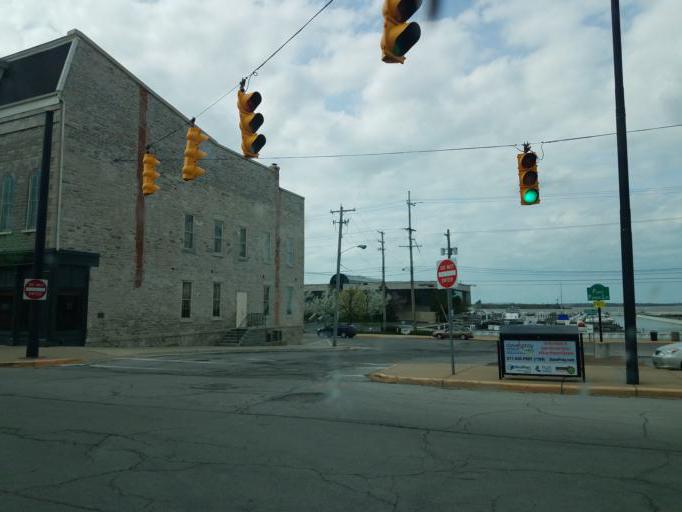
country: US
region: Ohio
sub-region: Erie County
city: Sandusky
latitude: 41.4577
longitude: -82.7107
